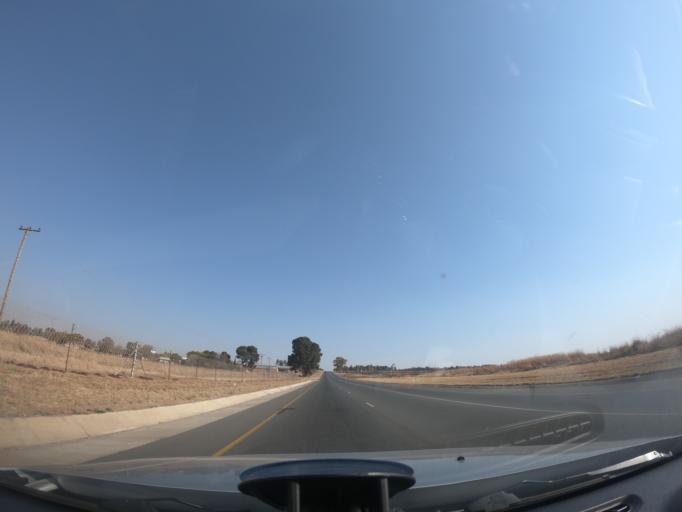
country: ZA
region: Gauteng
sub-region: City of Johannesburg Metropolitan Municipality
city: Diepsloot
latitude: -25.8615
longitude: 28.0342
